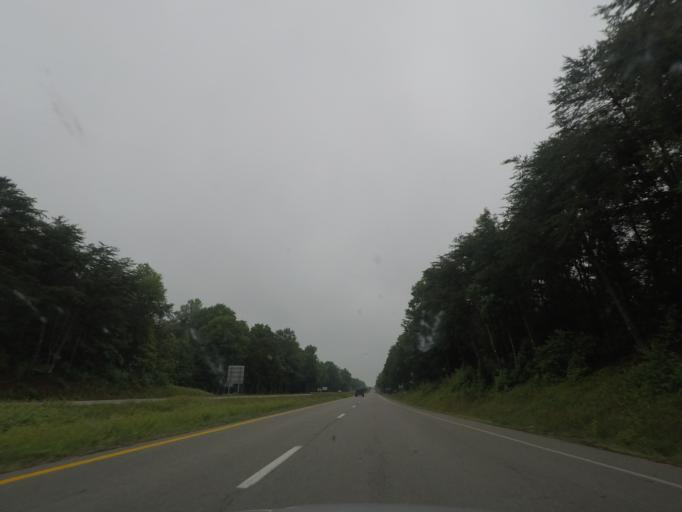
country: US
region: Virginia
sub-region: Charlotte County
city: Charlotte Court House
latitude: 37.0382
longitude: -78.4702
